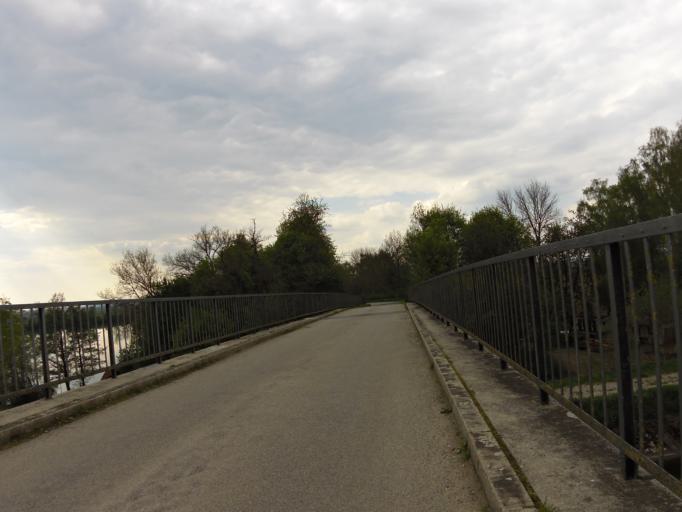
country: DE
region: Bavaria
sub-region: Upper Bavaria
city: Wartenberg
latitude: 48.4025
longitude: 11.9629
